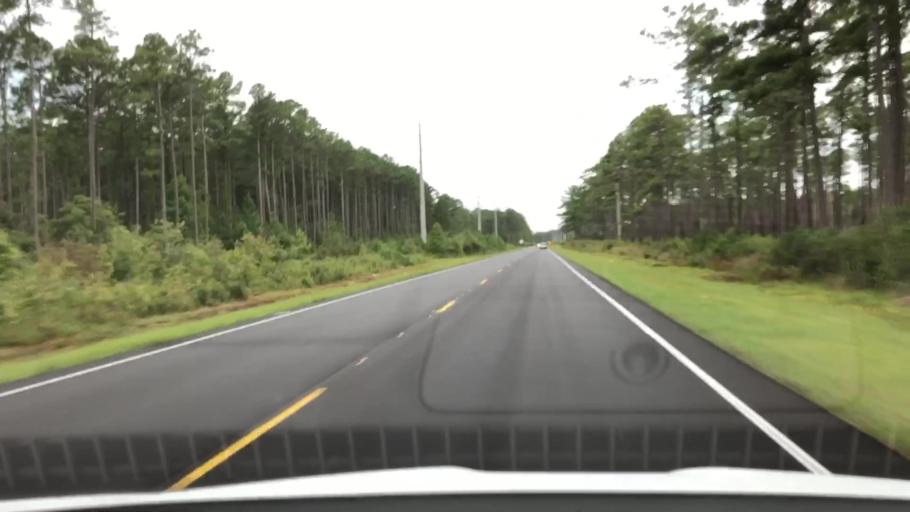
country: US
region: North Carolina
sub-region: Onslow County
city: Swansboro
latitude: 34.7778
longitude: -77.1040
